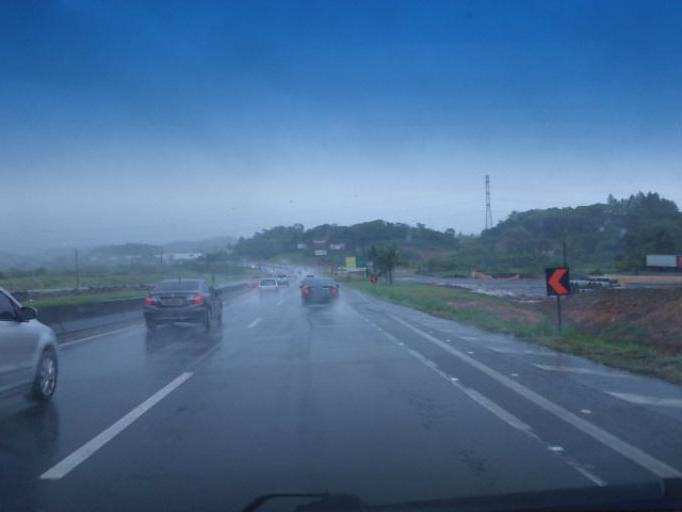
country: BR
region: Santa Catarina
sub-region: Joinville
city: Joinville
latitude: -26.3991
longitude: -48.8396
